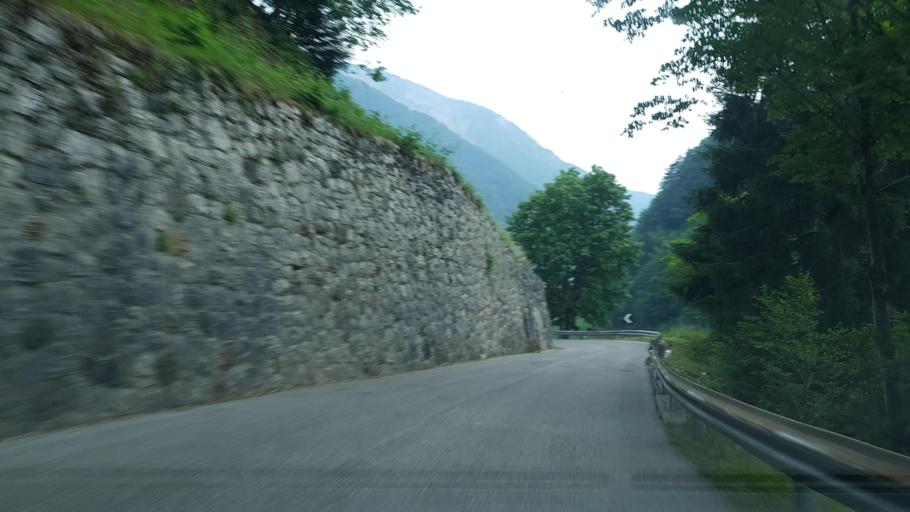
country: IT
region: Friuli Venezia Giulia
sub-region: Provincia di Udine
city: Pontebba
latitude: 46.5116
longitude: 13.3004
